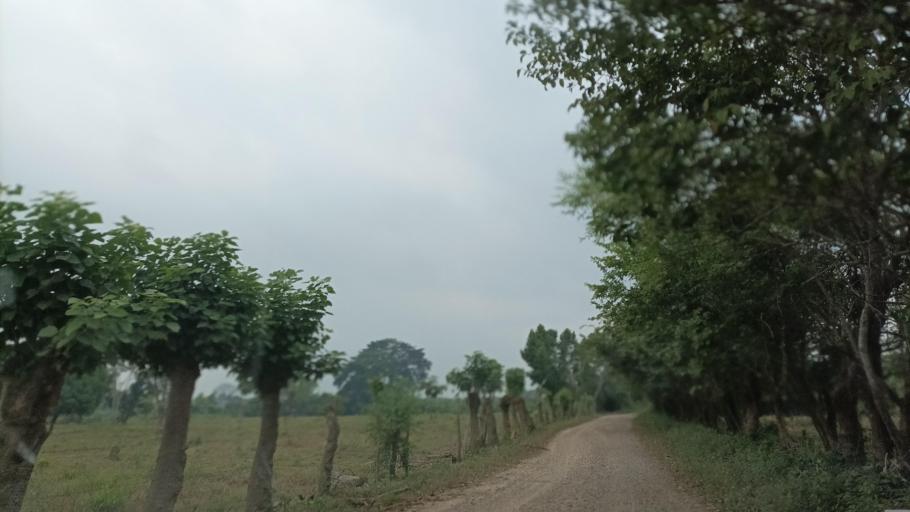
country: MX
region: Veracruz
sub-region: Uxpanapa
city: Poblado 10
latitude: 17.5642
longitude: -94.2240
